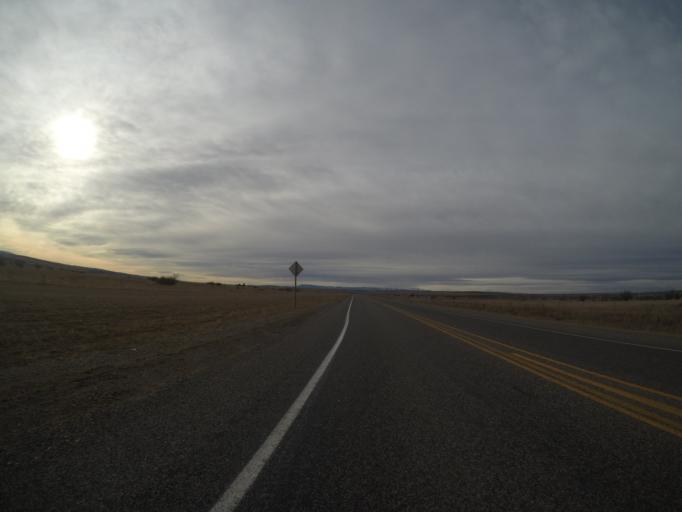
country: US
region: Montana
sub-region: Yellowstone County
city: Laurel
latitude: 45.5918
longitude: -108.8322
